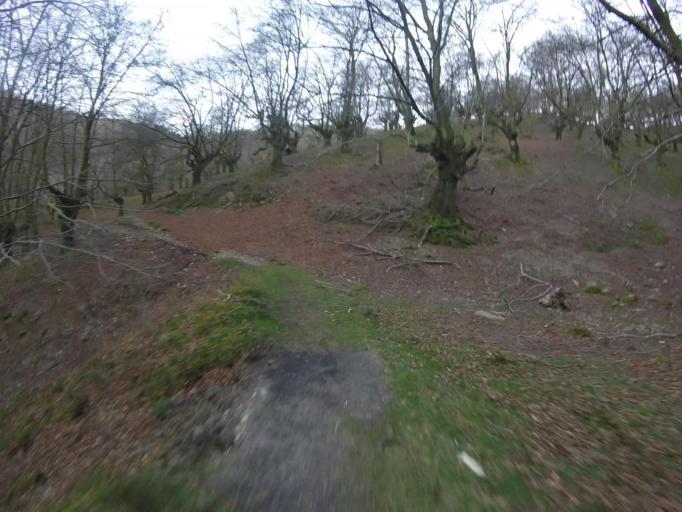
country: ES
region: Navarre
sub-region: Provincia de Navarra
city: Arano
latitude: 43.2523
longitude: -1.8220
